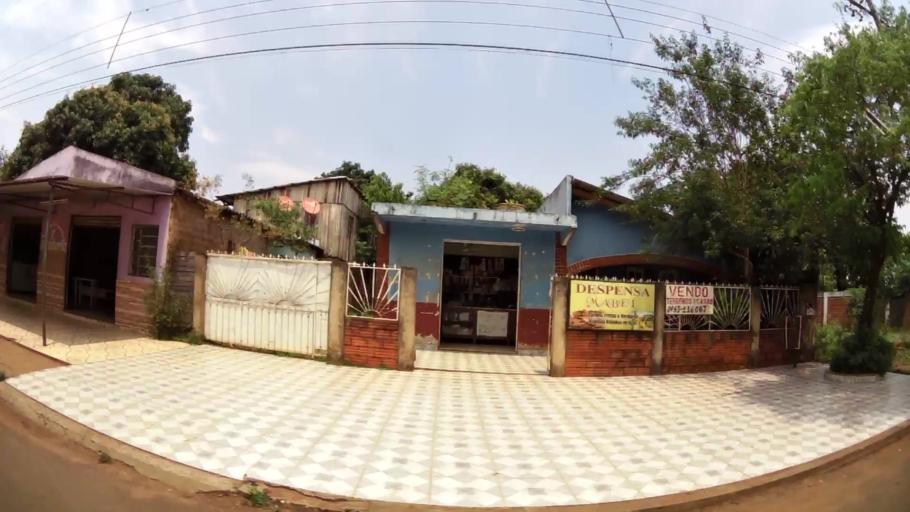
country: PY
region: Alto Parana
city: Ciudad del Este
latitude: -25.4967
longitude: -54.6283
